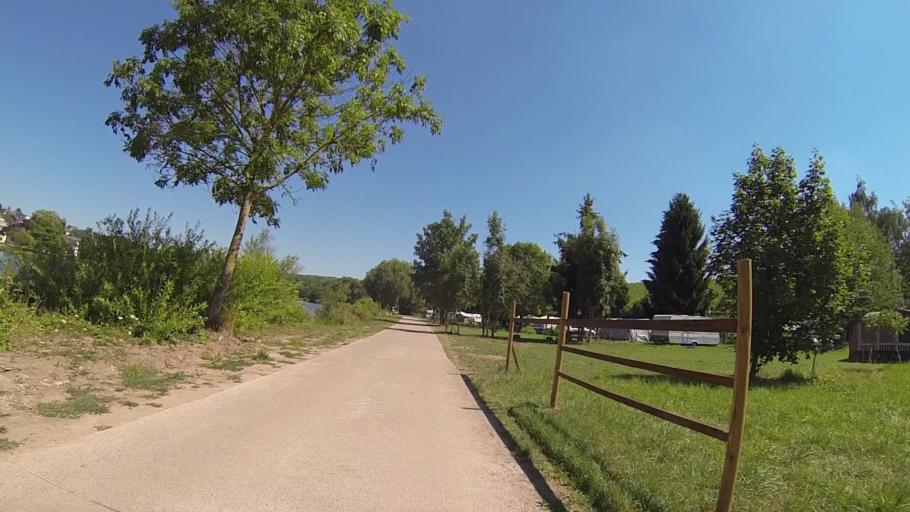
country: LU
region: Grevenmacher
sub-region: Canton de Remich
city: Remich
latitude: 49.5477
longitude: 6.3783
